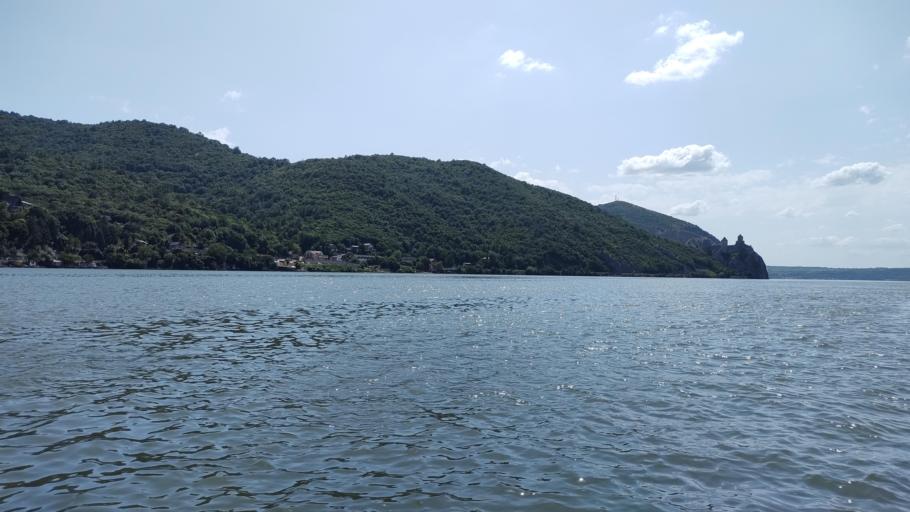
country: RO
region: Caras-Severin
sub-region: Comuna Pescari
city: Coronini
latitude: 44.6642
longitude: 21.6936
